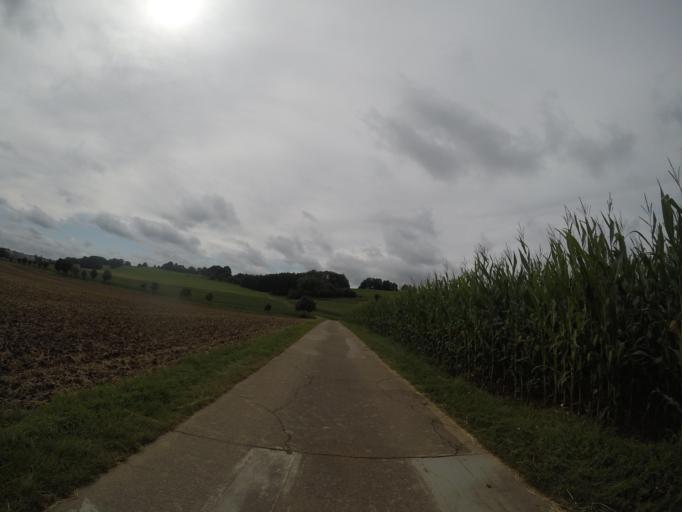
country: DE
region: Baden-Wuerttemberg
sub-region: Tuebingen Region
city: Laichingen
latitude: 48.4584
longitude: 9.6497
